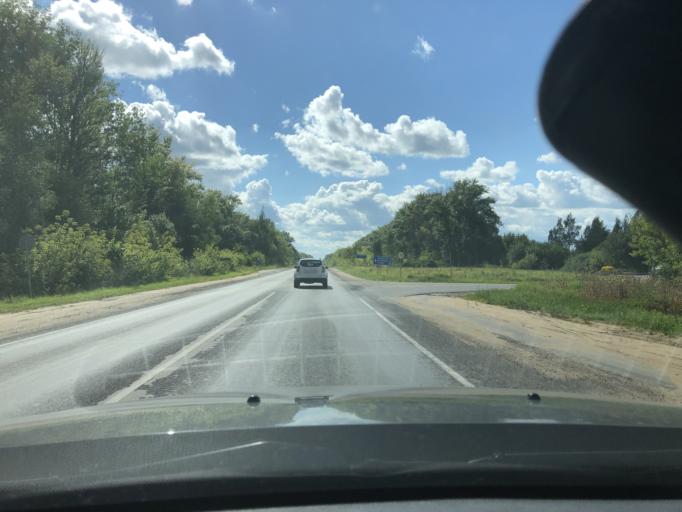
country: RU
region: Tula
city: Kimovsk
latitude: 53.9722
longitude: 38.5027
